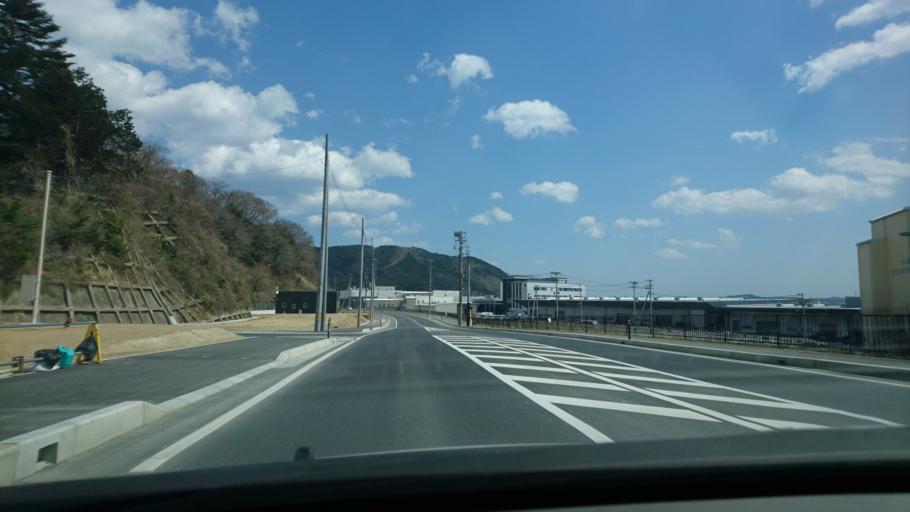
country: JP
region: Miyagi
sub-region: Oshika Gun
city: Onagawa Cho
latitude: 38.4463
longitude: 141.4493
